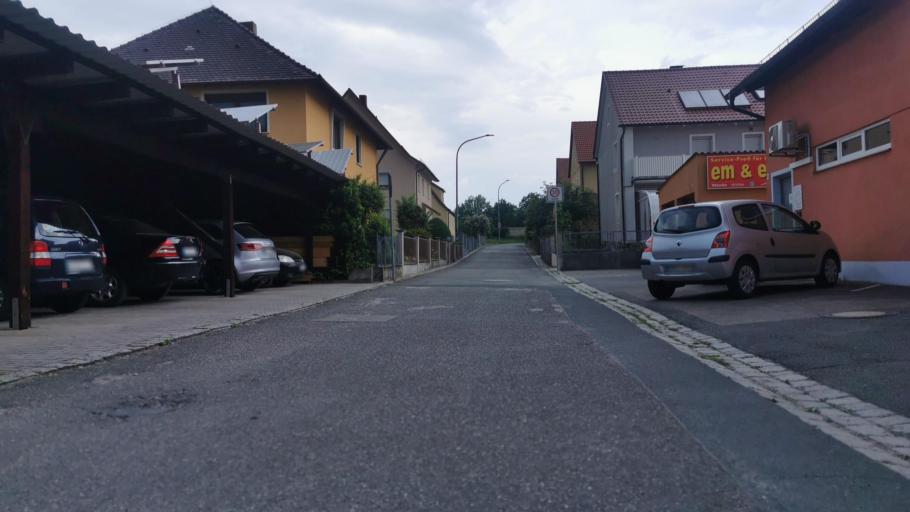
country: DE
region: Bavaria
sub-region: Regierungsbezirk Mittelfranken
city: Hochstadt an der Aisch
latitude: 49.7053
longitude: 10.8094
